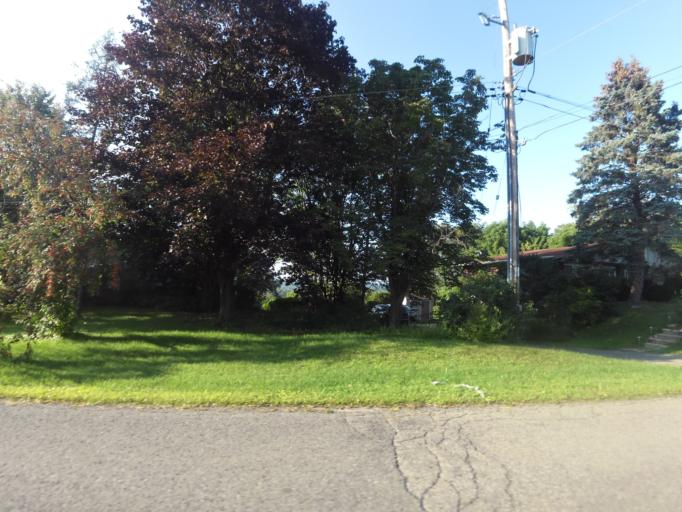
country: CA
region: Ontario
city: Clarence-Rockland
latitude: 45.5128
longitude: -75.4586
